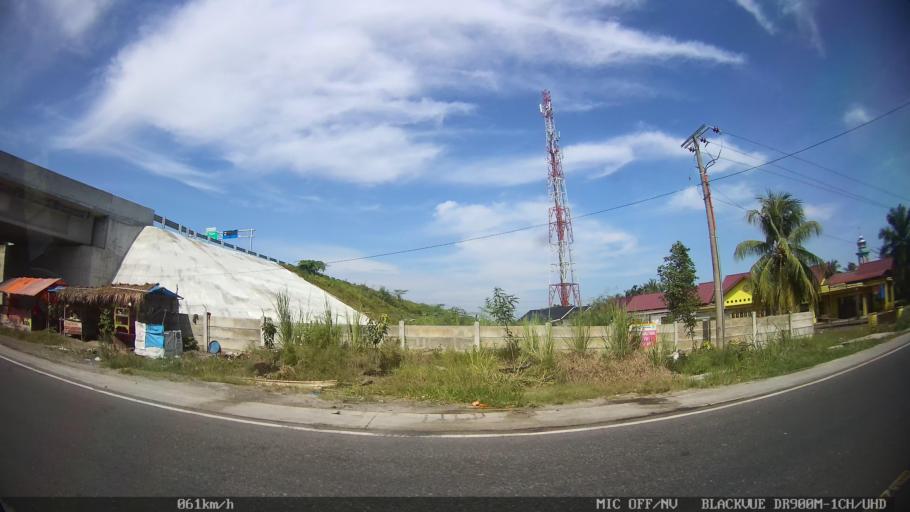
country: ID
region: North Sumatra
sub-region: Kabupaten Langkat
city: Stabat
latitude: 3.7144
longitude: 98.5040
